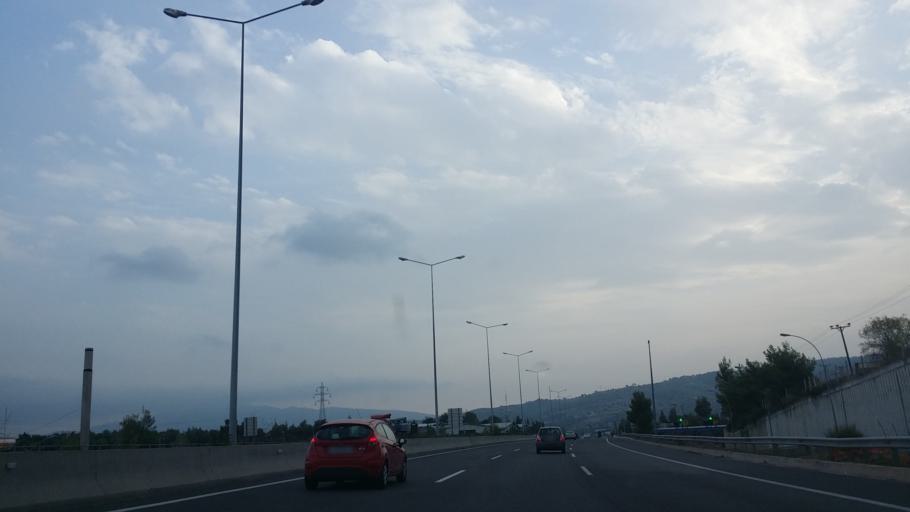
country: GR
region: Attica
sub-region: Nomarchia Anatolikis Attikis
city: Afidnes
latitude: 38.2044
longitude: 23.8548
